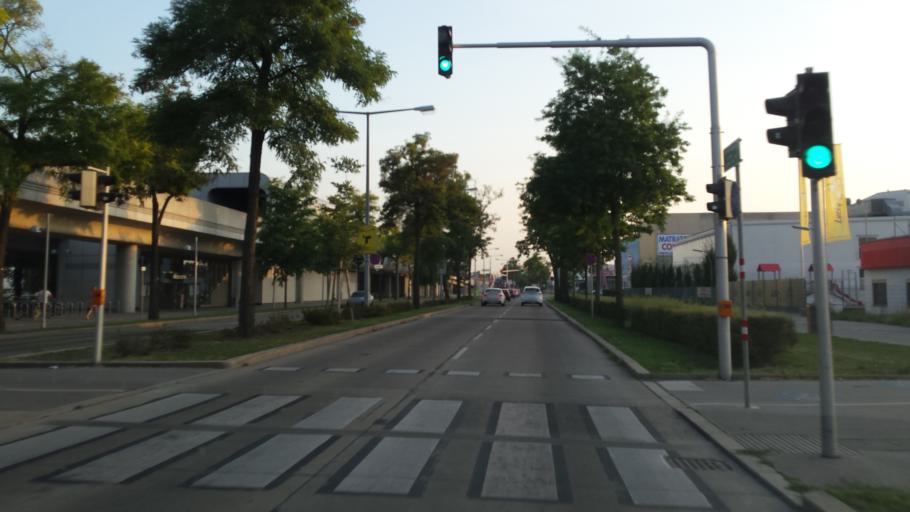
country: AT
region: Lower Austria
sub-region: Politischer Bezirk Wien-Umgebung
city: Gerasdorf bei Wien
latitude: 48.2590
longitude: 16.4501
